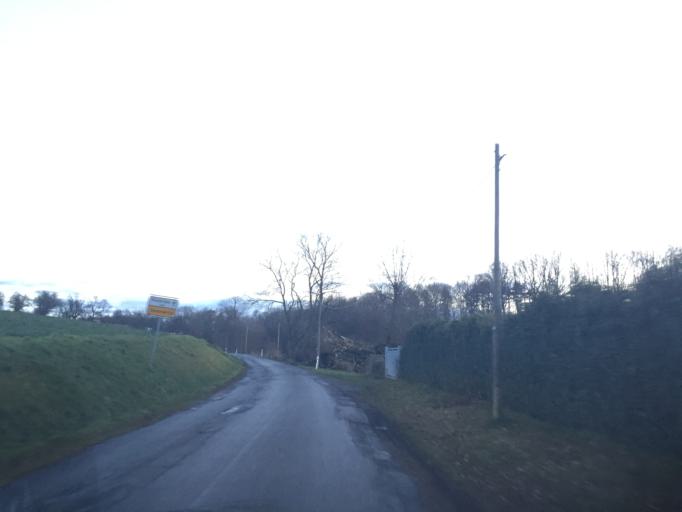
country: DE
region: Thuringia
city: Schmolln
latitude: 50.8753
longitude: 12.3314
